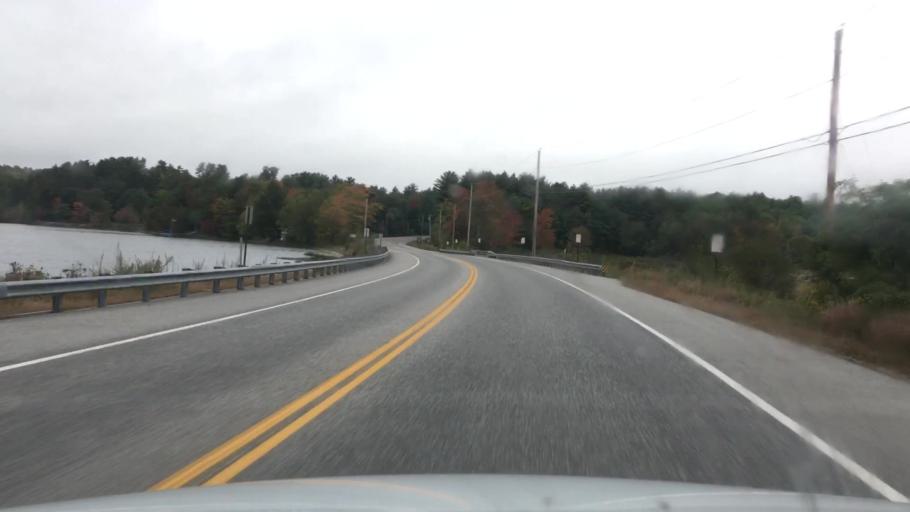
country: US
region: Maine
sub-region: Androscoggin County
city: Poland
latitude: 44.0373
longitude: -70.3715
